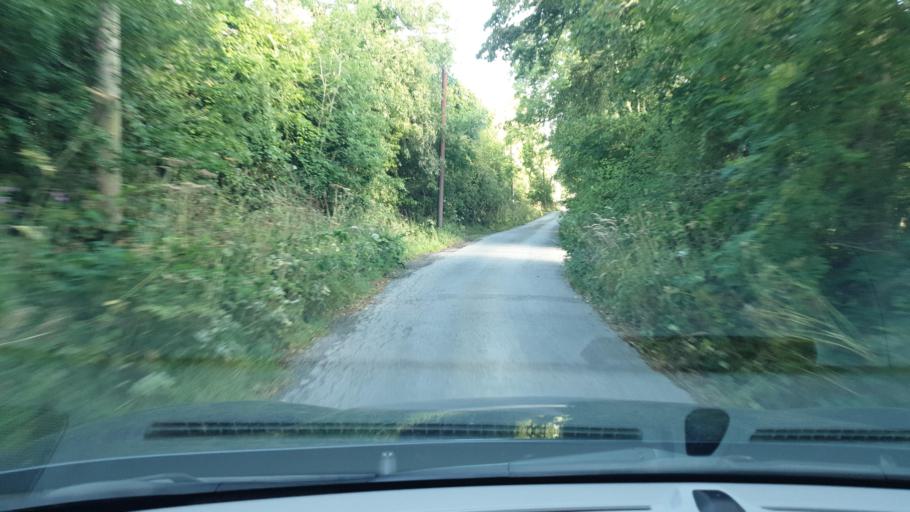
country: IE
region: Leinster
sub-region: An Mhi
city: Stamullin
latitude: 53.5973
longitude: -6.2638
